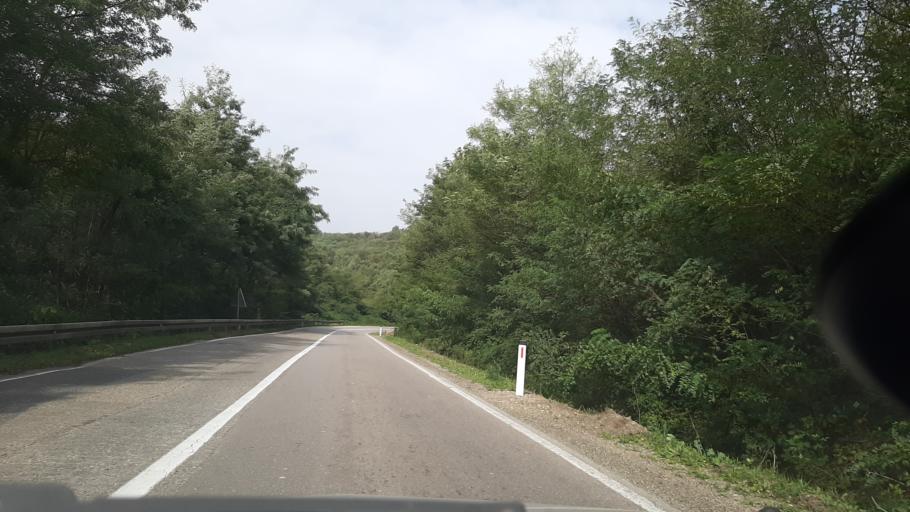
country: BA
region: Republika Srpska
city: Laktasi
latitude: 44.8742
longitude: 17.3630
